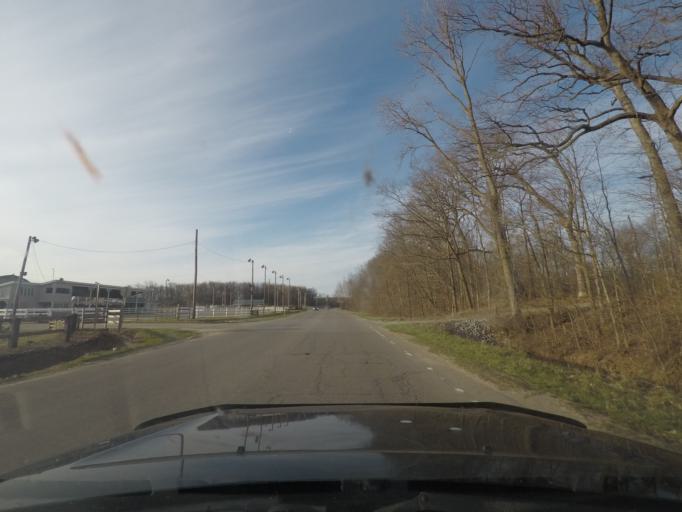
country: US
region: Indiana
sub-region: LaPorte County
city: LaPorte
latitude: 41.5961
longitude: -86.7492
